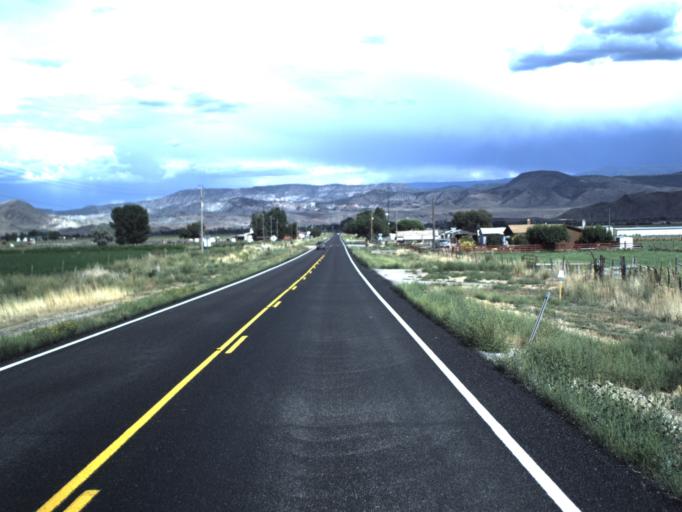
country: US
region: Utah
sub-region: Sevier County
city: Richfield
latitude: 38.7725
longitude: -112.0662
